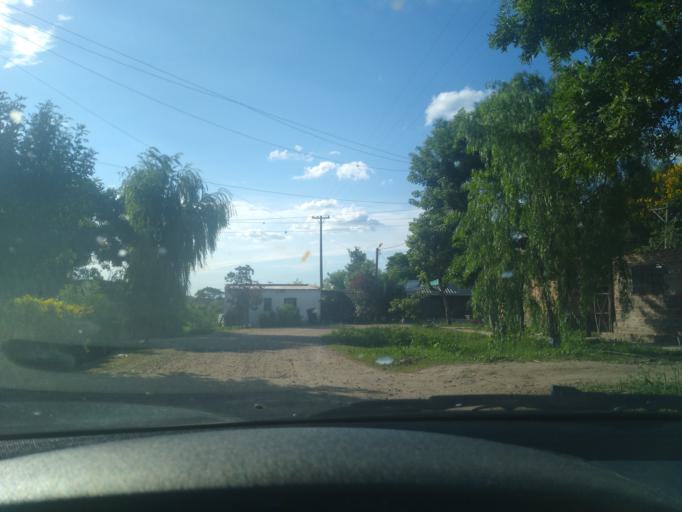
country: AR
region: Chaco
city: Barranqueras
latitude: -27.4714
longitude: -58.9349
